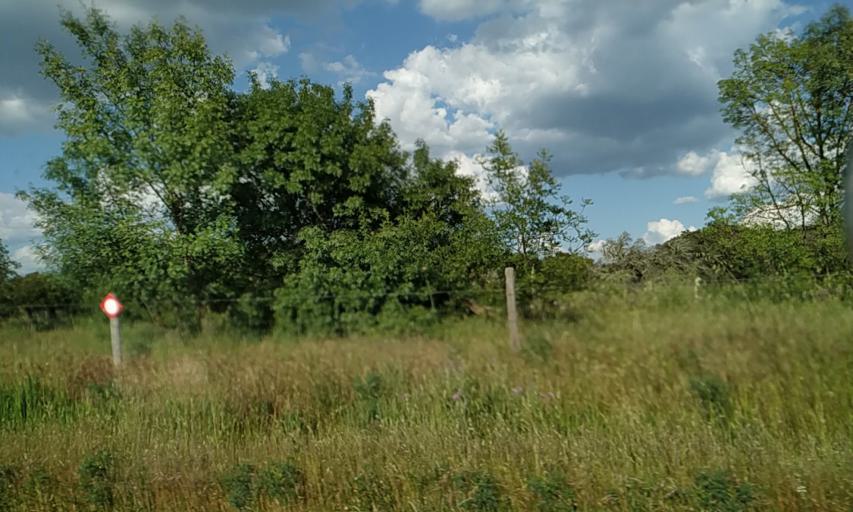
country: PT
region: Portalegre
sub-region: Portalegre
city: Urra
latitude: 39.2089
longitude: -7.4585
